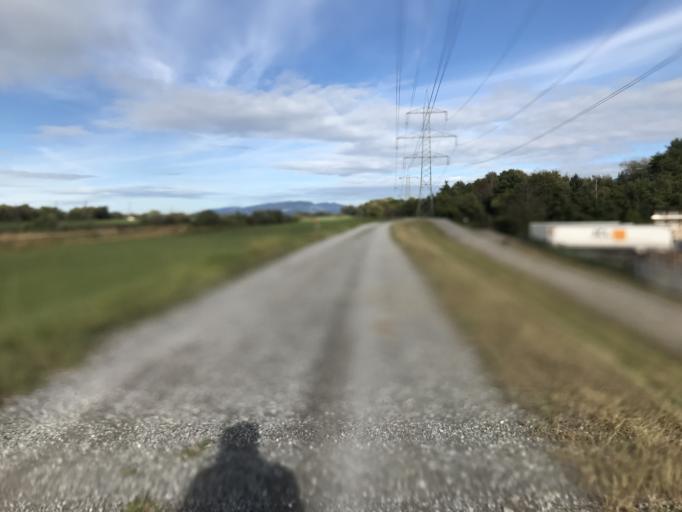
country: AT
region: Vorarlberg
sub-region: Politischer Bezirk Feldkirch
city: Mader
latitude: 47.3602
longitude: 9.6184
